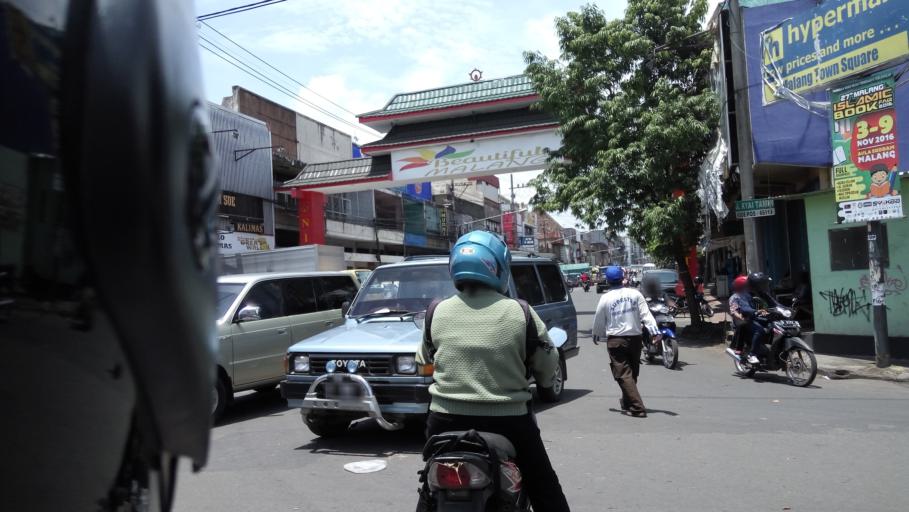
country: ID
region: East Java
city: Malang
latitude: -7.9892
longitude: 112.6349
